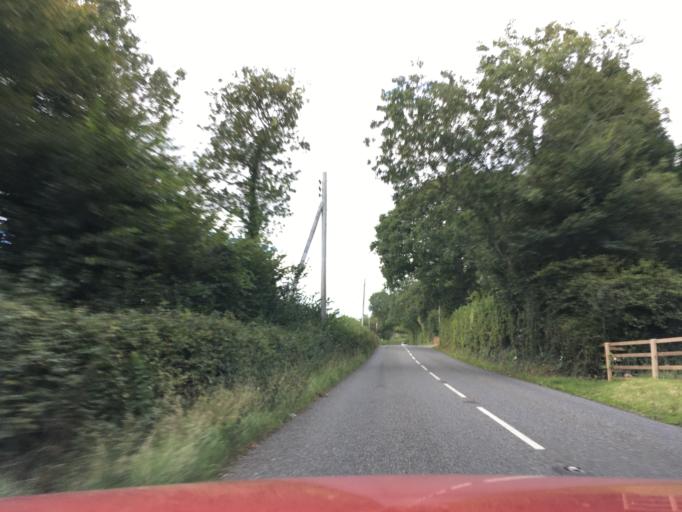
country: GB
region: England
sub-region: Devon
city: Sidmouth
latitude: 50.7354
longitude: -3.2132
